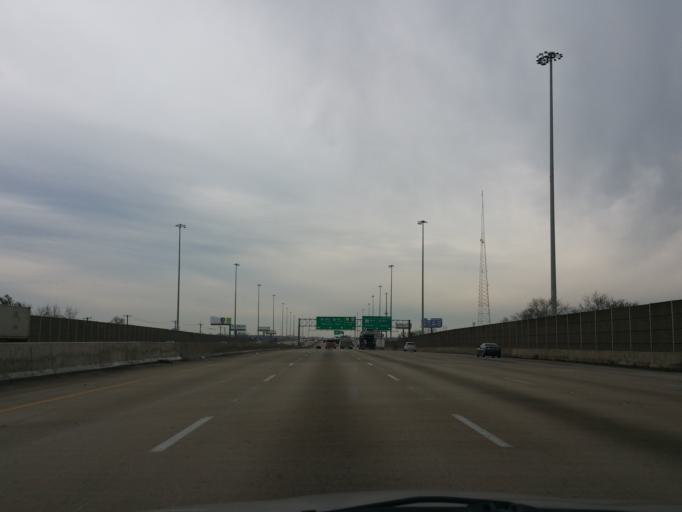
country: US
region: Illinois
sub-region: Cook County
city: Lansing
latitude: 41.5779
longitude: -87.5395
